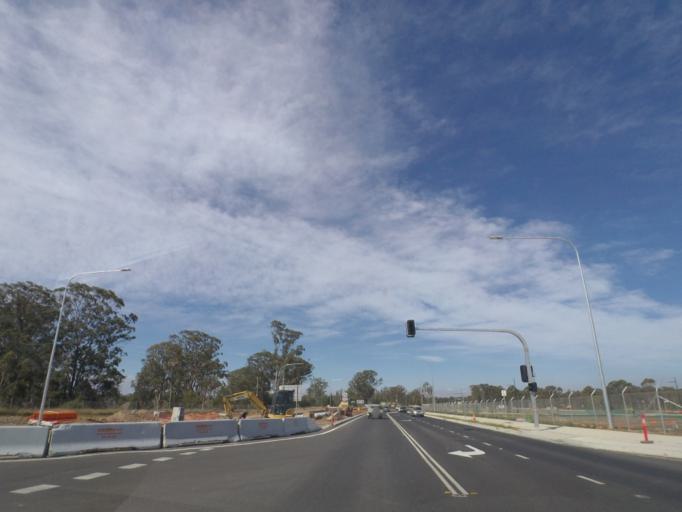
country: AU
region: New South Wales
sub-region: Campbelltown Municipality
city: Denham Court
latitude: -33.9733
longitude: 150.8602
